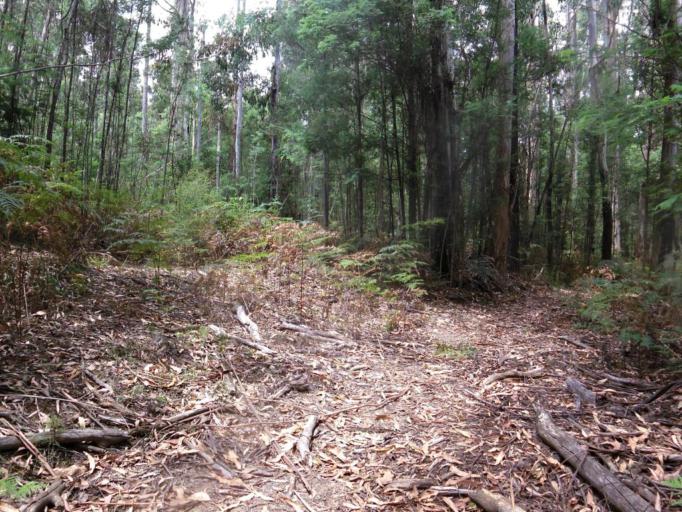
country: AU
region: Victoria
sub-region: Yarra Ranges
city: Healesville
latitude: -37.4438
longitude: 145.5836
